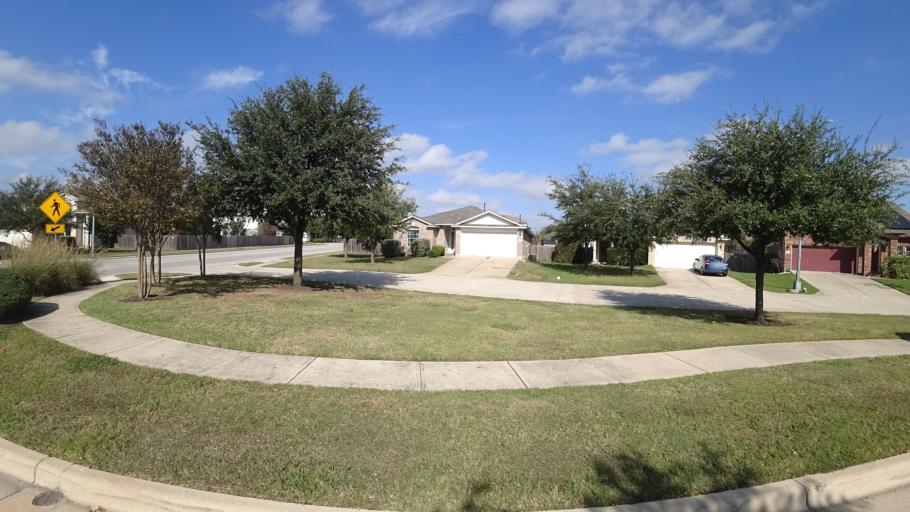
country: US
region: Texas
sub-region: Travis County
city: Pflugerville
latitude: 30.4202
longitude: -97.6394
